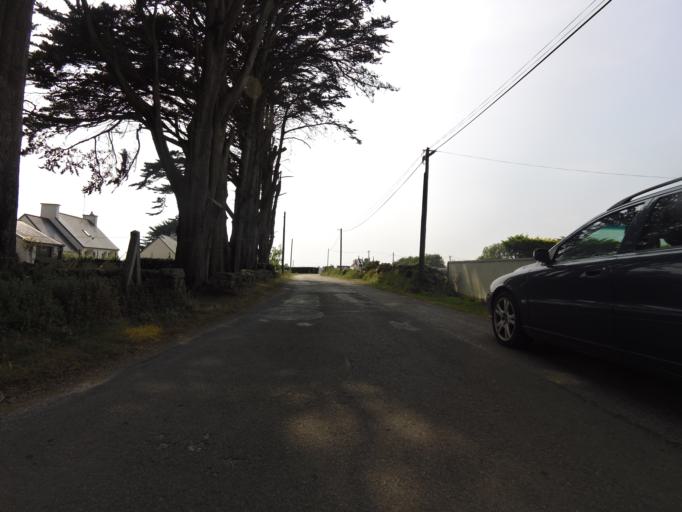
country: FR
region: Brittany
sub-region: Departement du Finistere
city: Esquibien
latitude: 48.0177
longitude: -4.5881
